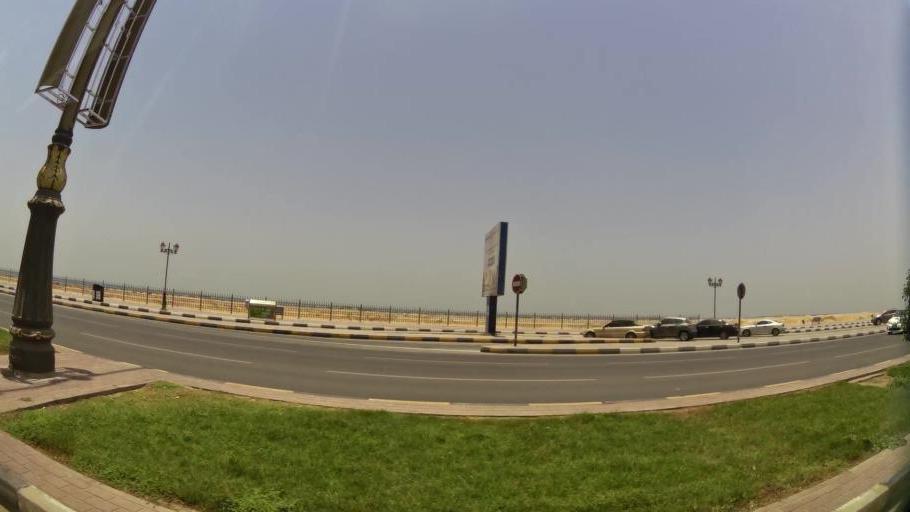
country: AE
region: Ajman
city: Ajman
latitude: 25.4112
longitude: 55.4349
